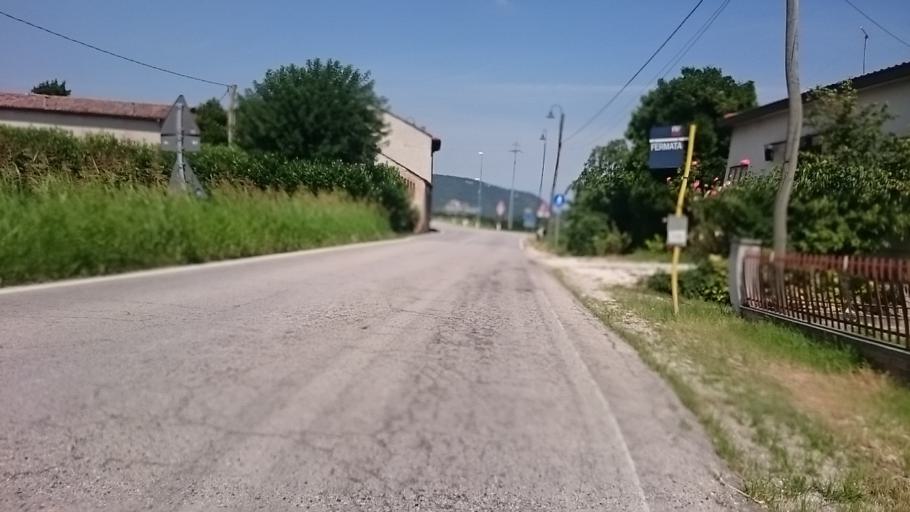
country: IT
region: Veneto
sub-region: Provincia di Vicenza
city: Villaganzerla
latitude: 45.4465
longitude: 11.6385
